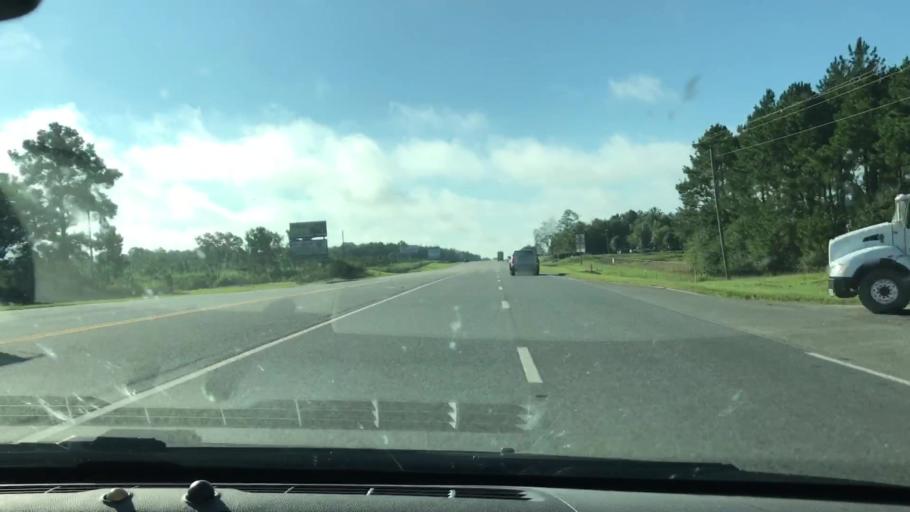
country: US
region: Georgia
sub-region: Terrell County
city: Dawson
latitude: 31.7559
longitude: -84.4266
